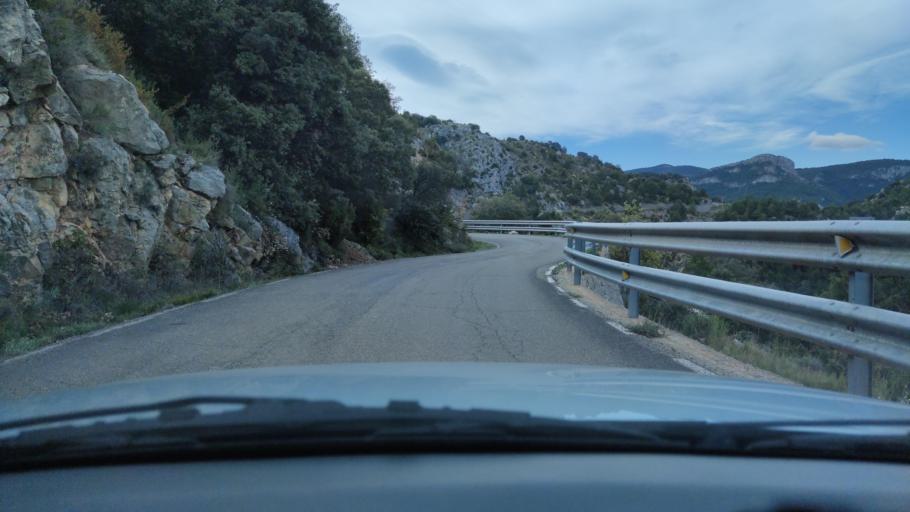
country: ES
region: Catalonia
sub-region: Provincia de Lleida
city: Coll de Nargo
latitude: 42.2449
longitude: 1.3685
